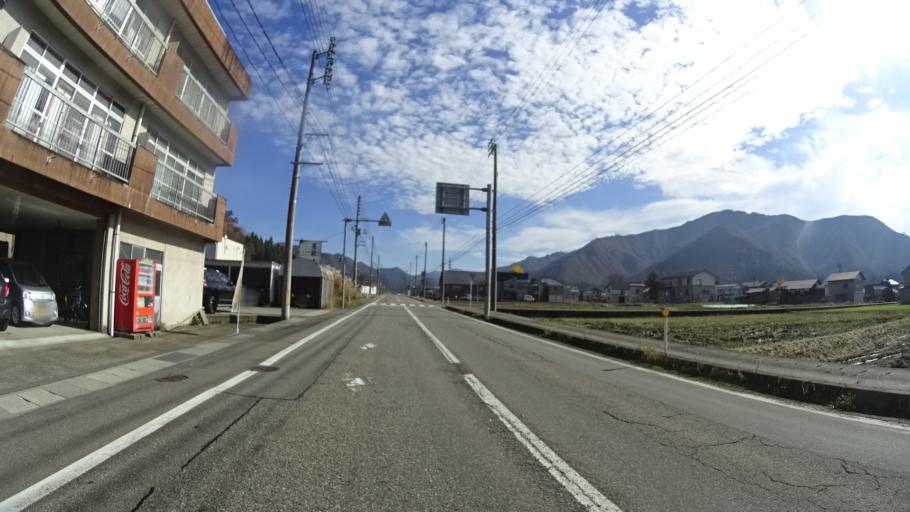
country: JP
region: Niigata
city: Muikamachi
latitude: 37.2284
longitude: 138.9882
